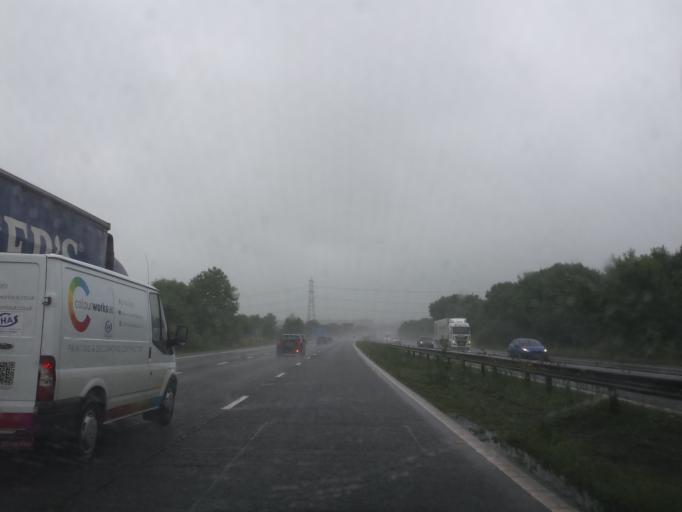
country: GB
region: England
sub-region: Leicestershire
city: Kirby Muxloe
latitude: 52.6487
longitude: -1.2326
